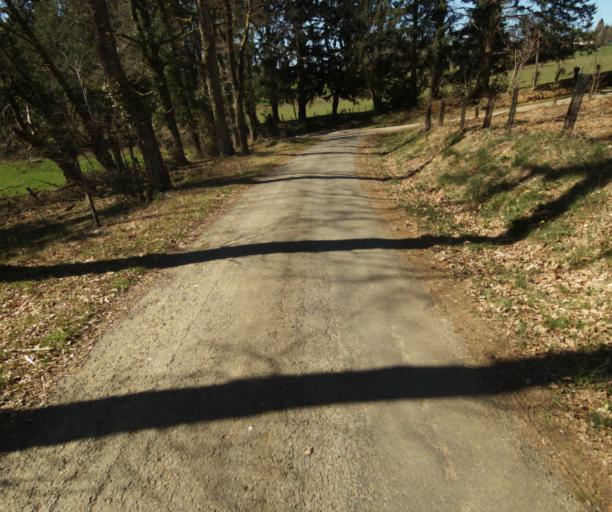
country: FR
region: Limousin
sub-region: Departement de la Correze
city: Seilhac
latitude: 45.3810
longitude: 1.6861
